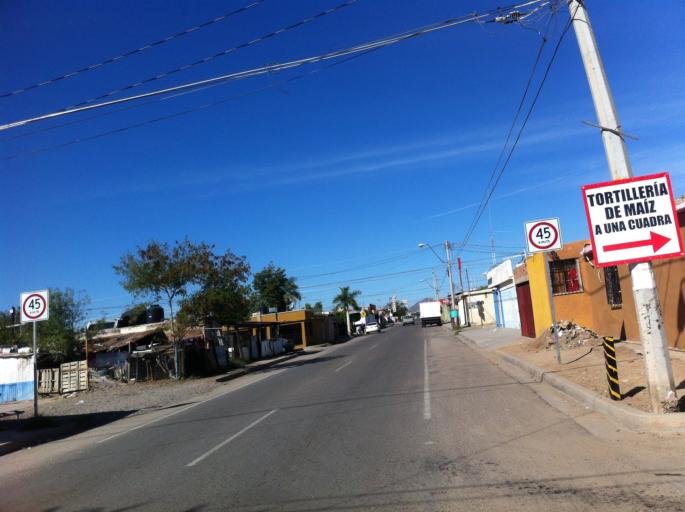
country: MX
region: Sonora
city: Hermosillo
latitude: 29.1084
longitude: -111.0114
